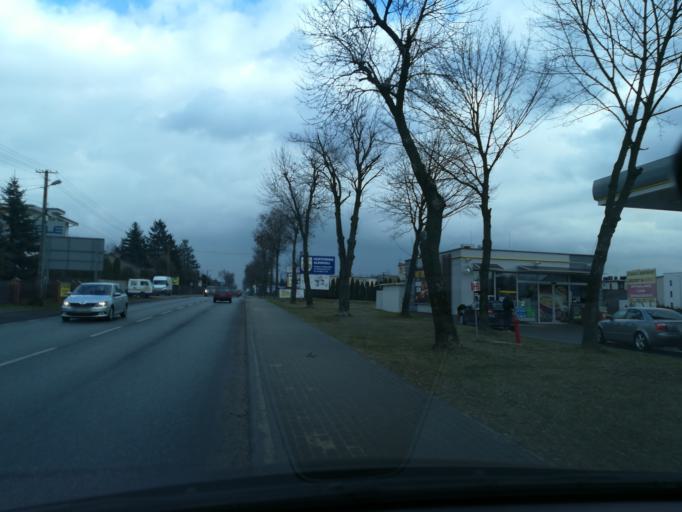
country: PL
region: Lodz Voivodeship
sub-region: Powiat radomszczanski
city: Radomsko
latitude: 51.0740
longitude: 19.4124
